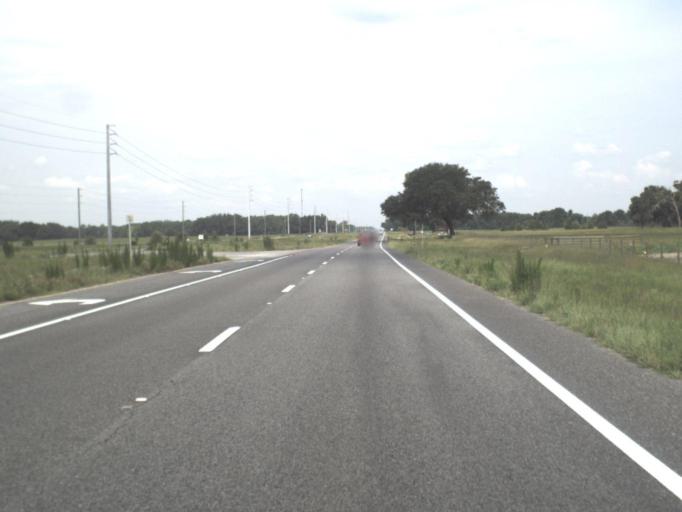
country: US
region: Florida
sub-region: Levy County
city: Bronson
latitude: 29.4753
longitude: -82.7471
